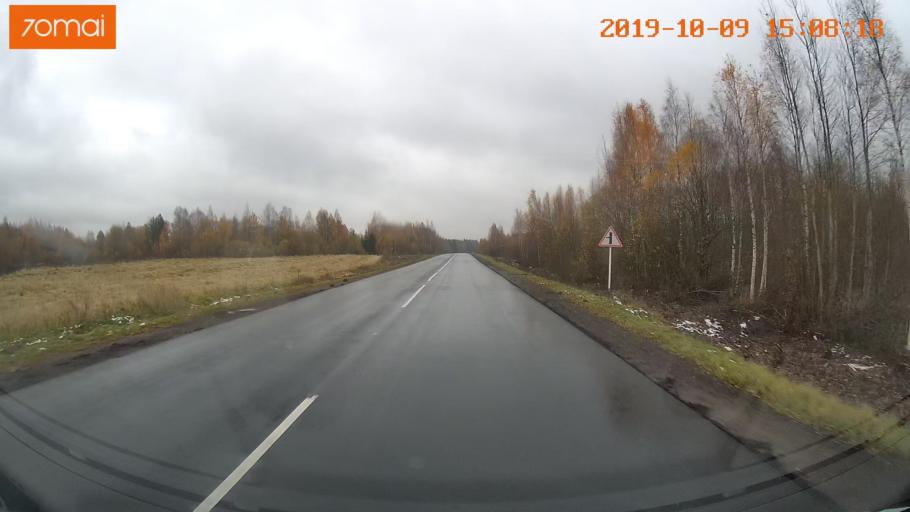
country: RU
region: Kostroma
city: Susanino
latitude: 58.2079
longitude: 41.6491
